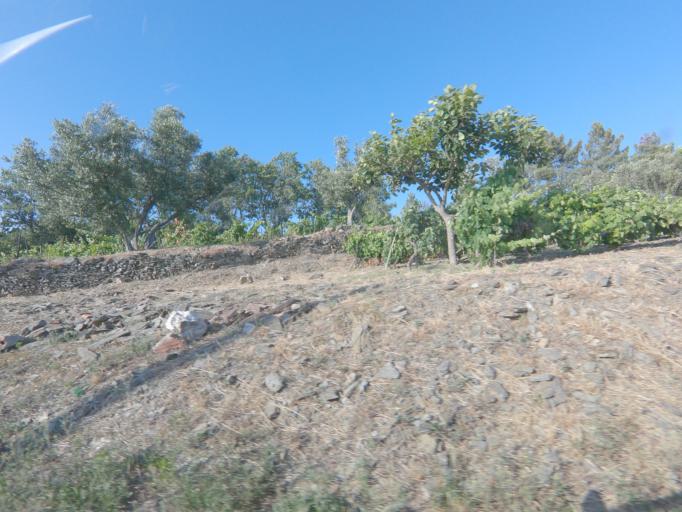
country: PT
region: Vila Real
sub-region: Sabrosa
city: Vilela
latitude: 41.1781
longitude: -7.6082
